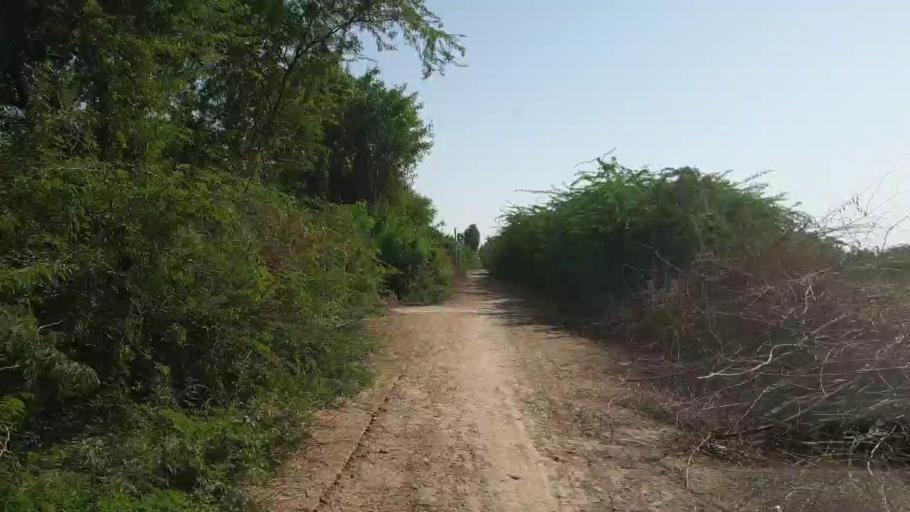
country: PK
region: Sindh
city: Kadhan
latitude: 24.5838
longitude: 69.0117
